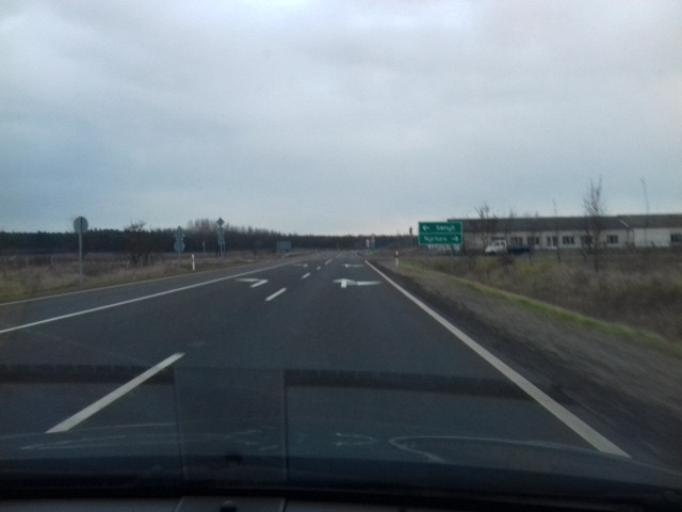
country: HU
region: Szabolcs-Szatmar-Bereg
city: Nyirpazony
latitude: 48.0127
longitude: 21.8439
